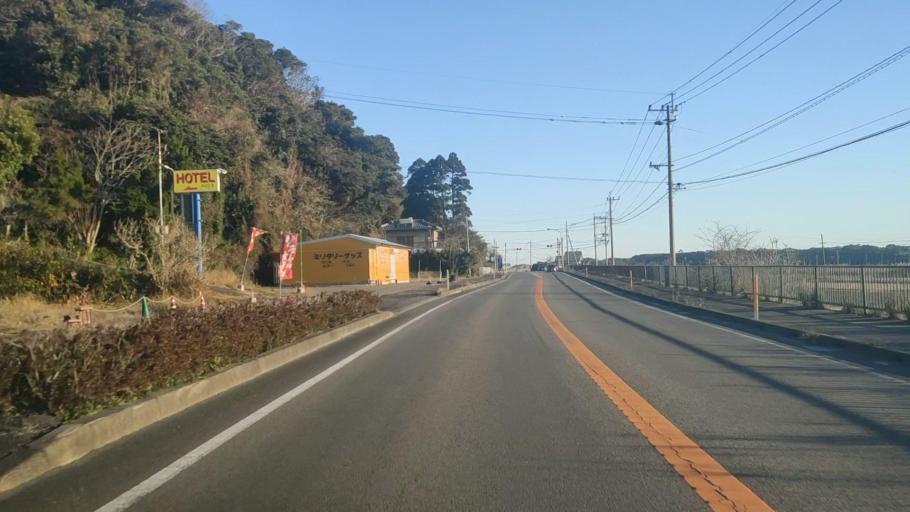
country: JP
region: Miyazaki
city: Takanabe
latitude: 32.0943
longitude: 131.5162
